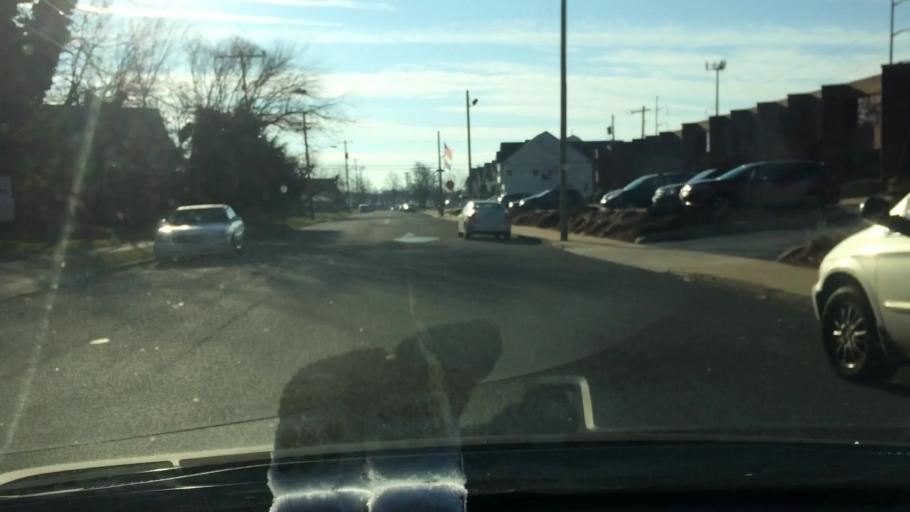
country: US
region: Pennsylvania
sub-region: Montgomery County
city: Rockledge
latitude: 40.0813
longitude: -75.0323
